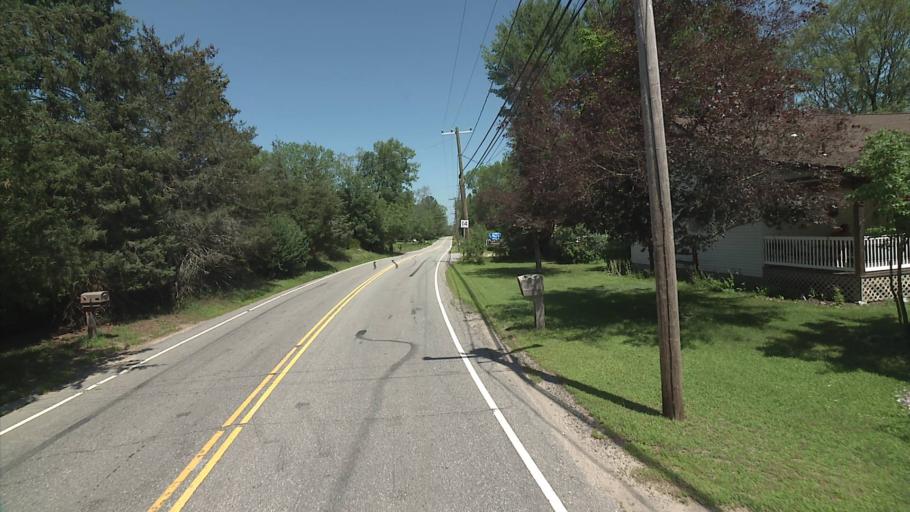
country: US
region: Connecticut
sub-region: Windham County
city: Moosup
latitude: 41.7125
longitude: -71.8445
